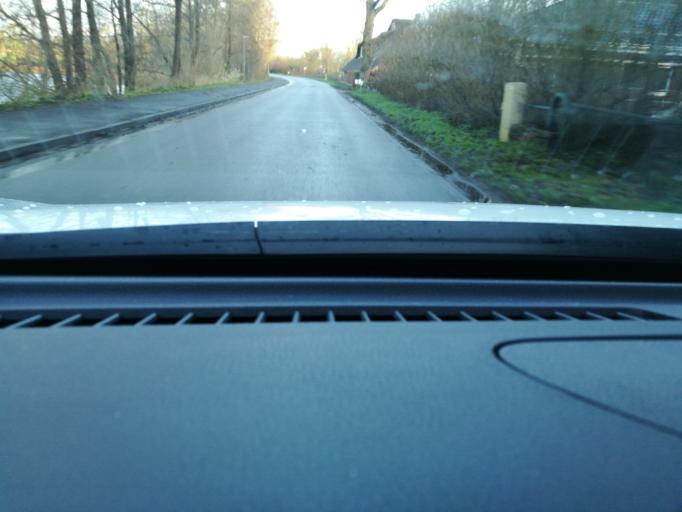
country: DE
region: Schleswig-Holstein
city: Holzbunge
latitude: 54.3955
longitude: 9.7052
